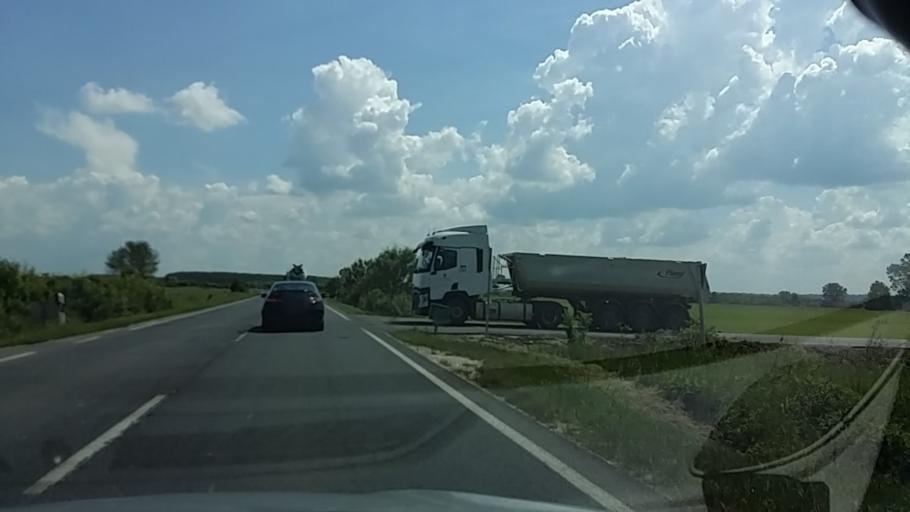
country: AT
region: Burgenland
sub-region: Politischer Bezirk Gussing
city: Heiligenbrunn
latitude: 46.9674
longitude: 16.4593
